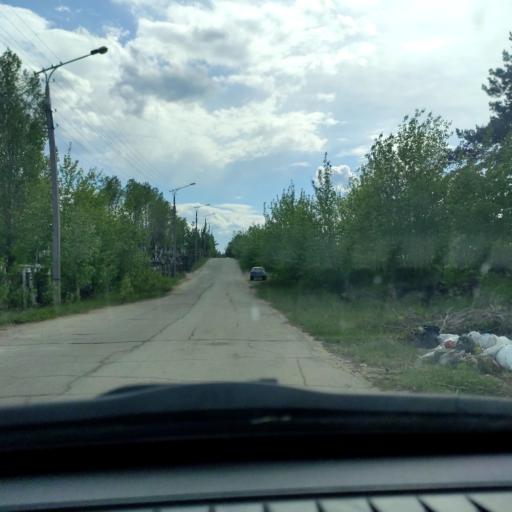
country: RU
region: Samara
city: Zhigulevsk
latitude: 53.5266
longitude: 49.5405
